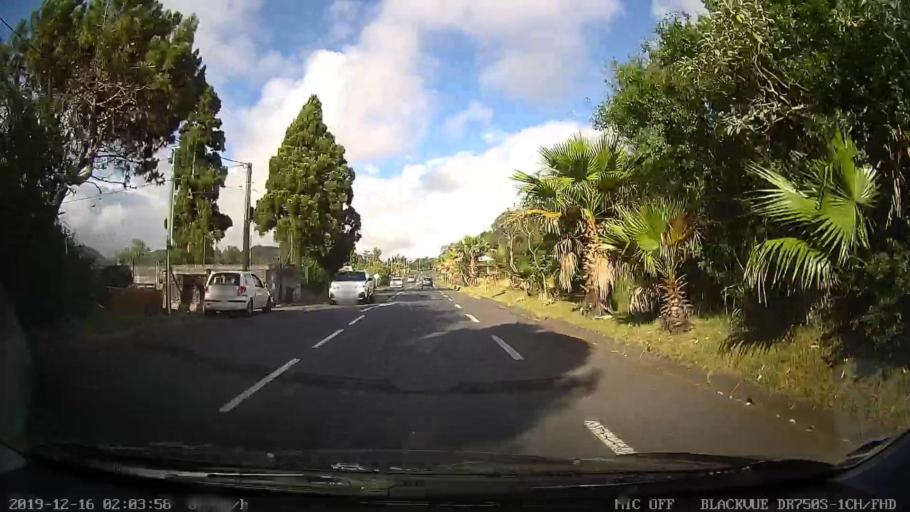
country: RE
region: Reunion
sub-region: Reunion
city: Le Tampon
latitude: -21.2067
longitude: 55.5683
